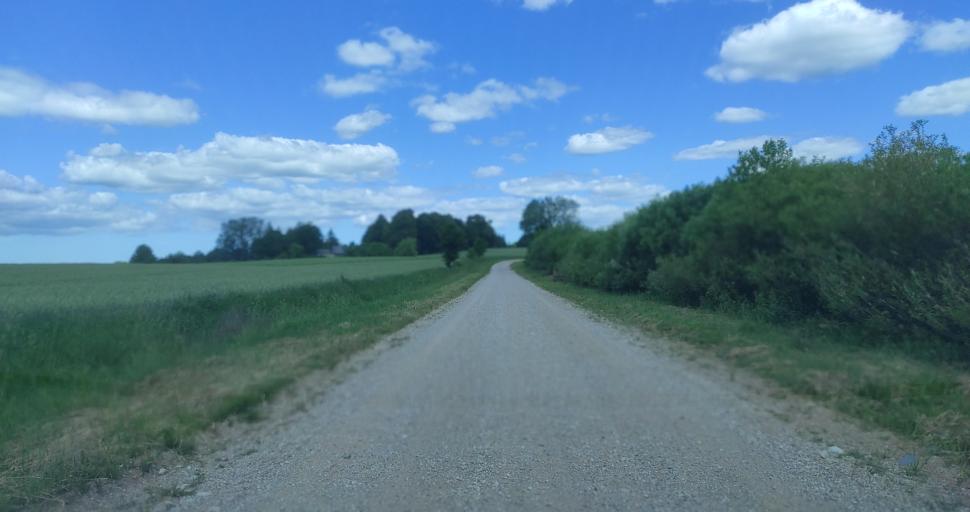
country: LV
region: Alsunga
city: Alsunga
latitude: 56.8694
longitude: 21.6967
